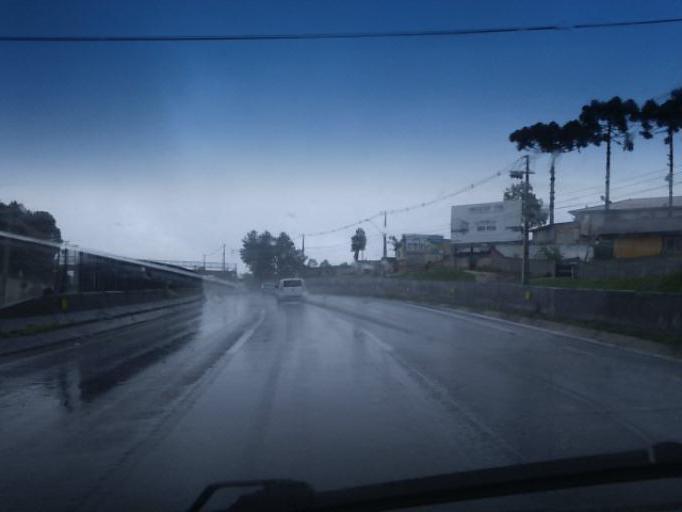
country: BR
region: Parana
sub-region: Sao Jose Dos Pinhais
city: Sao Jose dos Pinhais
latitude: -25.5868
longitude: -49.1730
